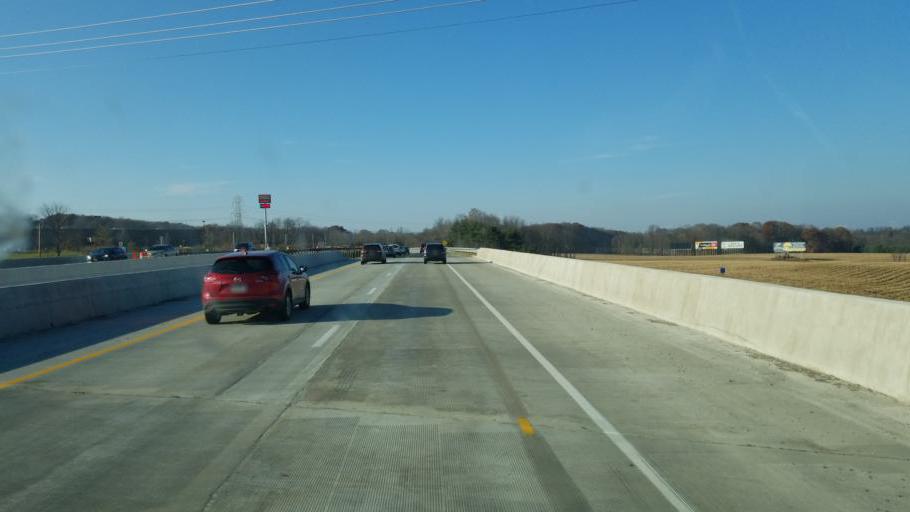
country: US
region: Ohio
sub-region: Medina County
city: Wadsworth
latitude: 41.0446
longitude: -81.6918
